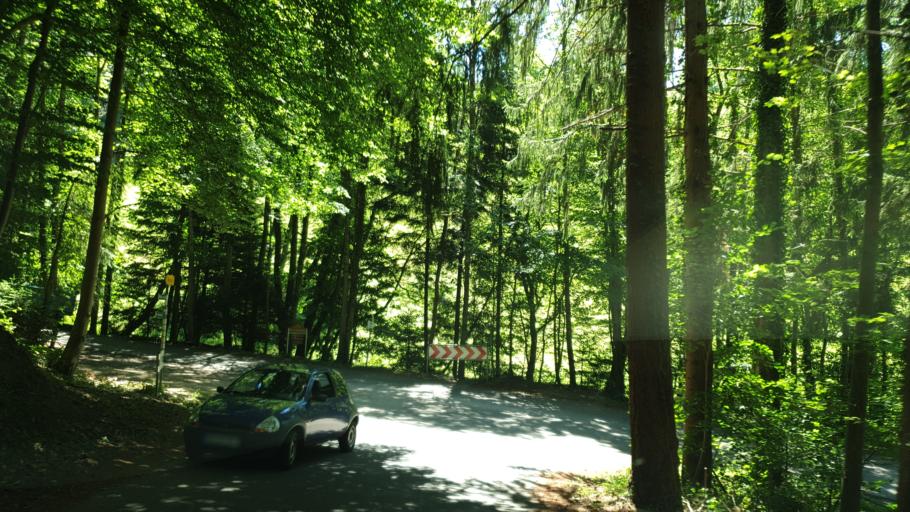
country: DE
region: Baden-Wuerttemberg
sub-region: Freiburg Region
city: Au
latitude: 47.9394
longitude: 7.8446
